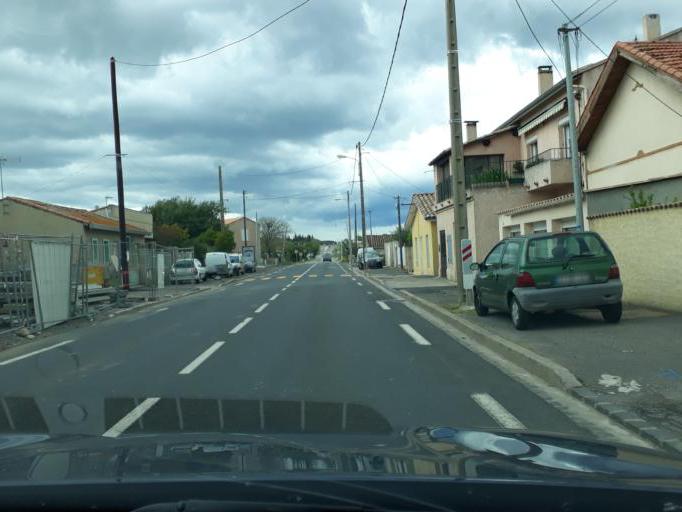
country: FR
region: Languedoc-Roussillon
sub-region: Departement de l'Herault
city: Bessan
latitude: 43.3659
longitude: 3.4235
